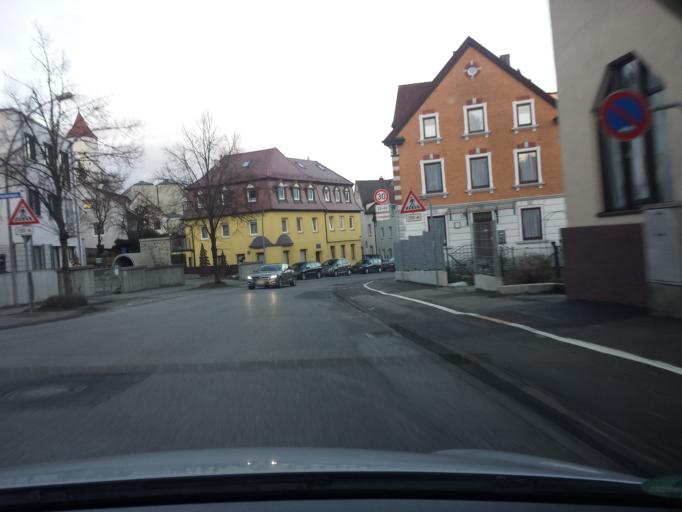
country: DE
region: Baden-Wuerttemberg
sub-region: Tuebingen Region
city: Biberach an der Riss
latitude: 48.0960
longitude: 9.7826
